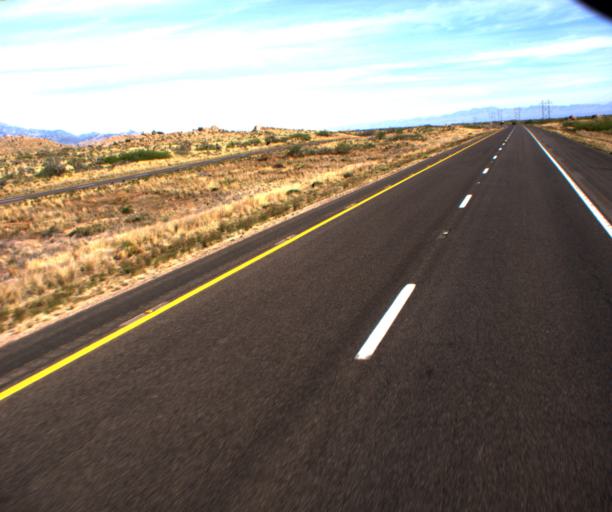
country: US
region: Arizona
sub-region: Graham County
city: Swift Trail Junction
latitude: 32.5182
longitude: -109.6736
